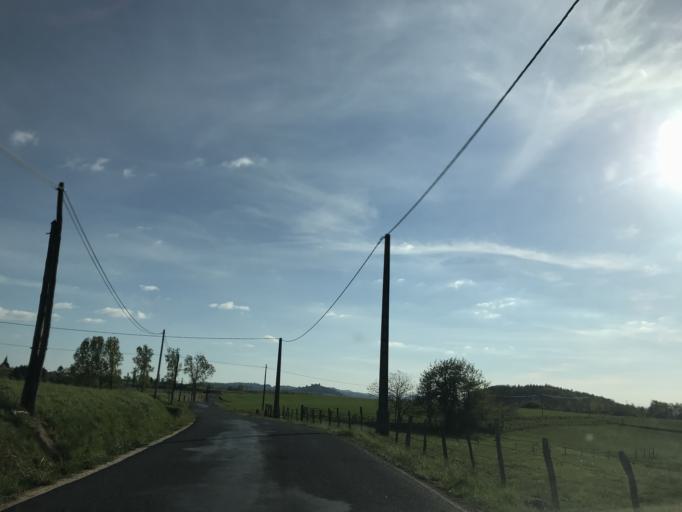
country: FR
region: Auvergne
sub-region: Departement du Puy-de-Dome
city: Courpiere
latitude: 45.7293
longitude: 3.4765
